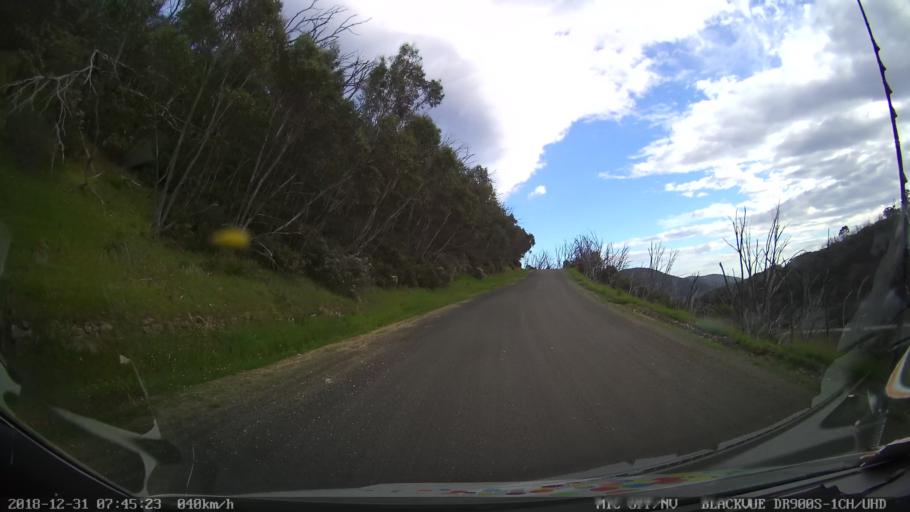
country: AU
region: New South Wales
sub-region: Snowy River
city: Jindabyne
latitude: -36.3647
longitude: 148.4031
